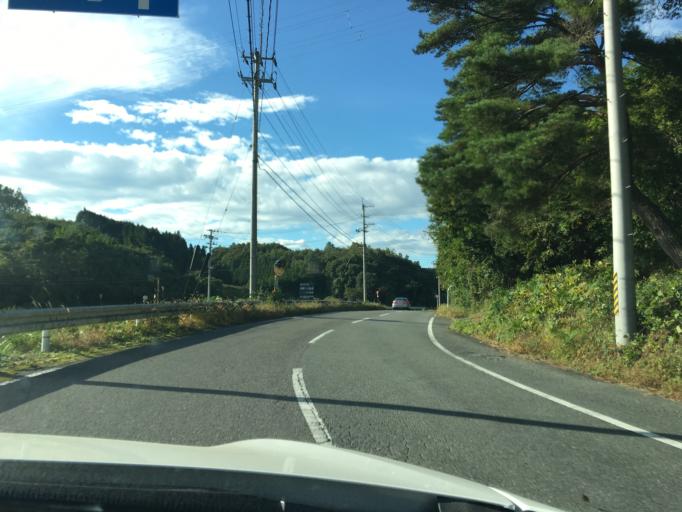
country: JP
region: Fukushima
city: Ishikawa
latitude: 37.1841
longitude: 140.4600
